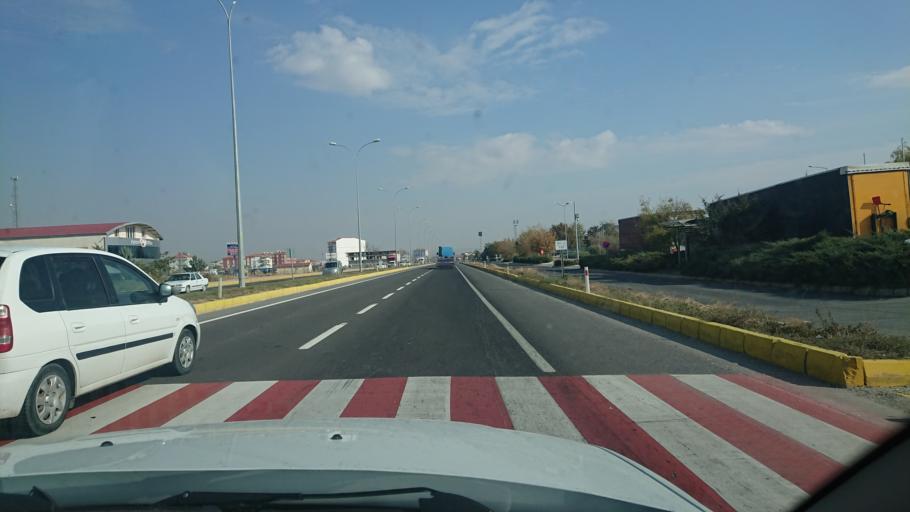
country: TR
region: Aksaray
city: Aksaray
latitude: 38.3505
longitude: 33.9627
